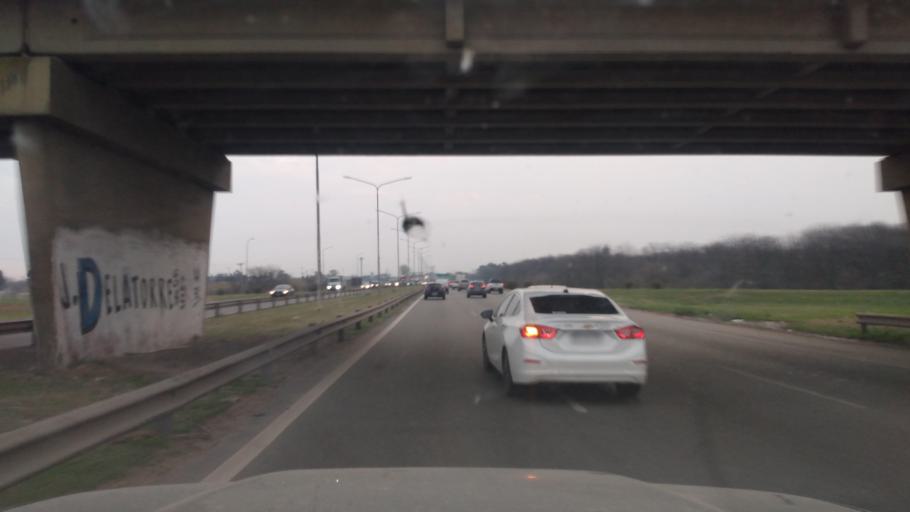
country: AR
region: Buenos Aires
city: Hurlingham
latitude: -34.5669
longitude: -58.6401
